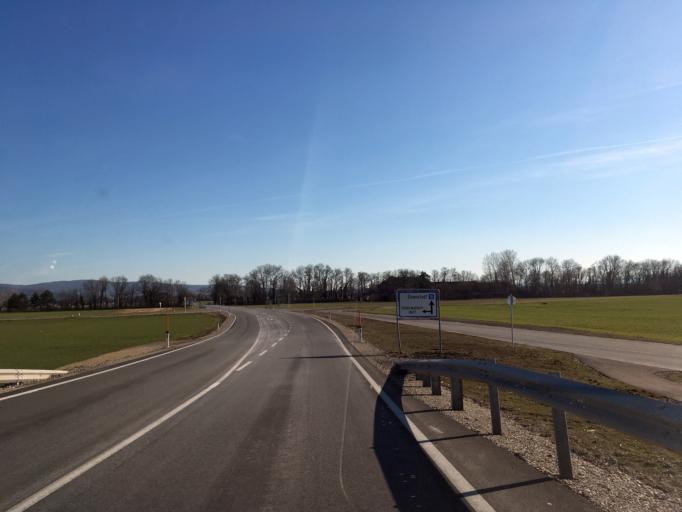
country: AT
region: Burgenland
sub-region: Eisenstadt-Umgebung
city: Wimpassing an der Leitha
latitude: 47.9335
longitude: 16.4201
